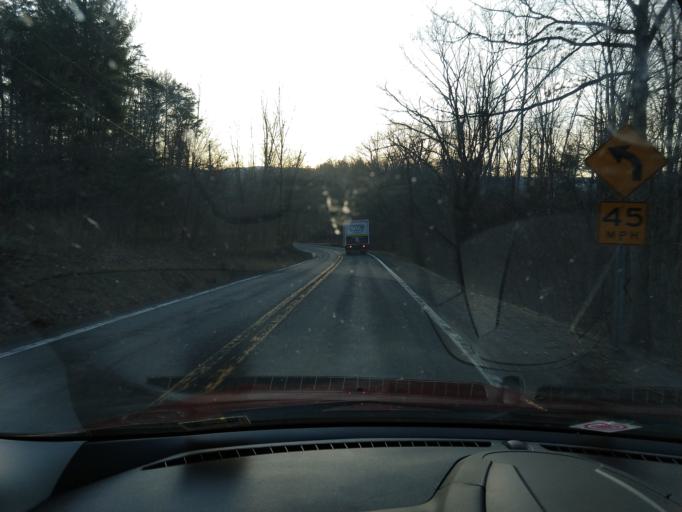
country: US
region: Virginia
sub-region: Frederick County
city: Shawnee Land
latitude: 39.4066
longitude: -78.4383
